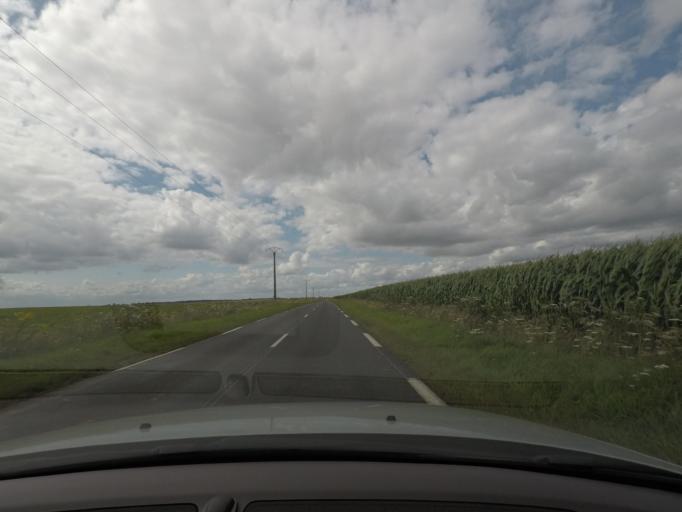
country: FR
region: Haute-Normandie
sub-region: Departement de l'Eure
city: Les Andelys
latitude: 49.2130
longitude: 1.4582
